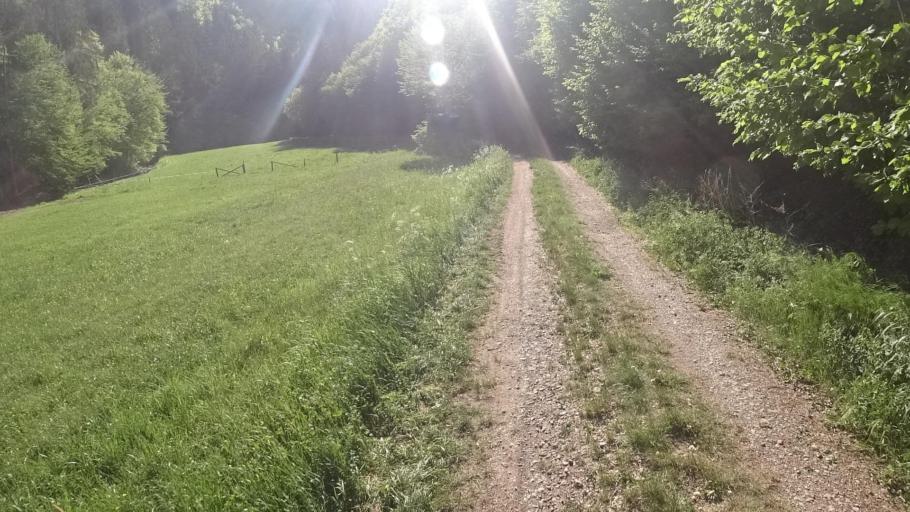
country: DE
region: Rheinland-Pfalz
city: Kirchsahr
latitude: 50.4929
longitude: 6.9007
